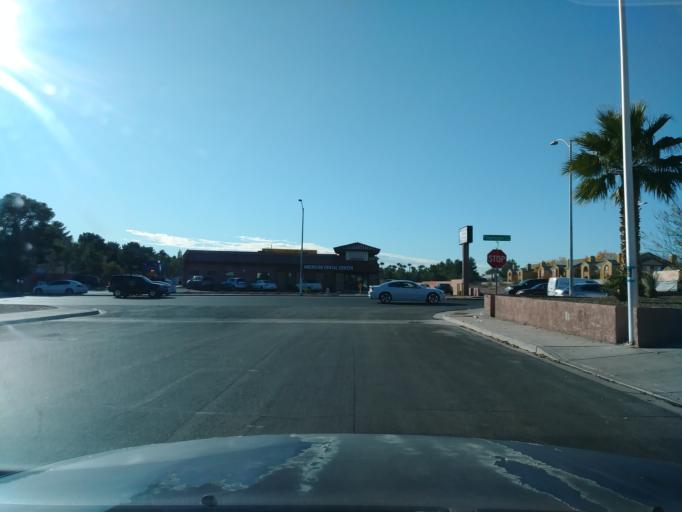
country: US
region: Nevada
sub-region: Clark County
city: Spring Valley
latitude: 36.1595
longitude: -115.2465
